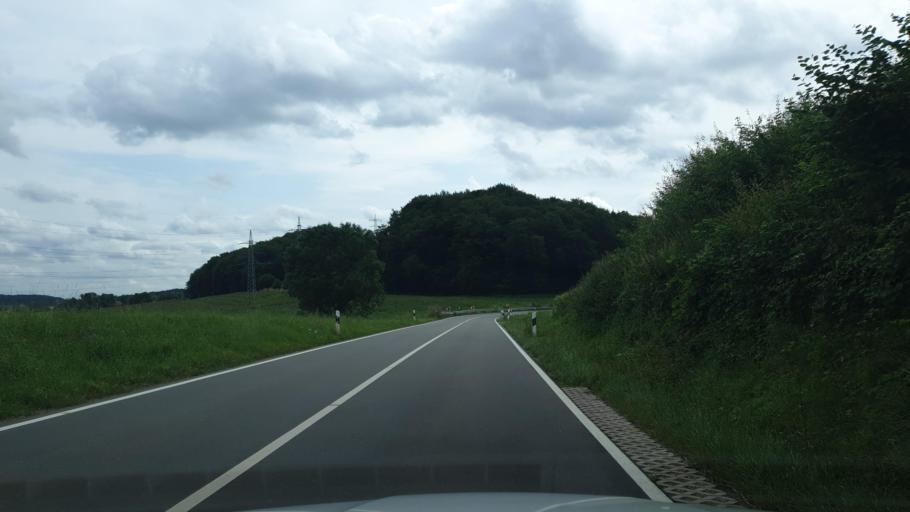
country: DE
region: Lower Saxony
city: Bissendorf
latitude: 52.2004
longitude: 8.1713
